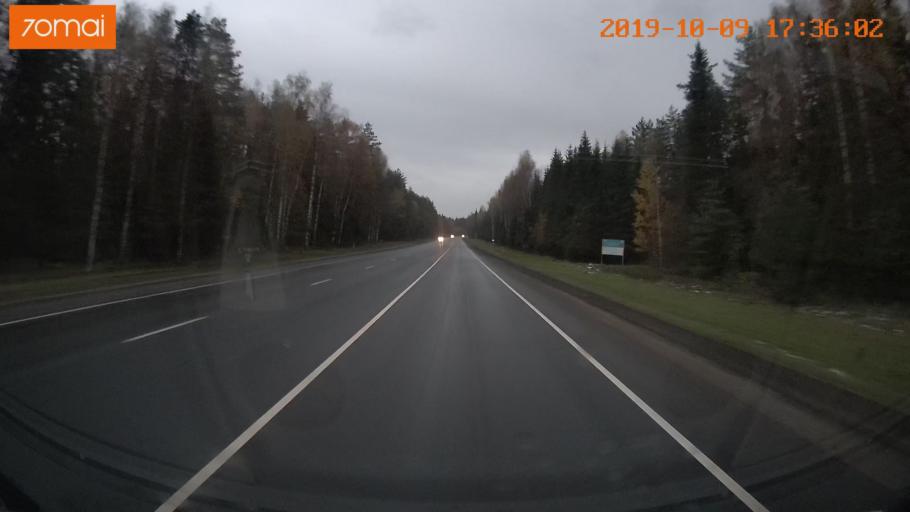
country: RU
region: Ivanovo
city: Bogorodskoye
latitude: 57.0844
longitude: 40.9985
